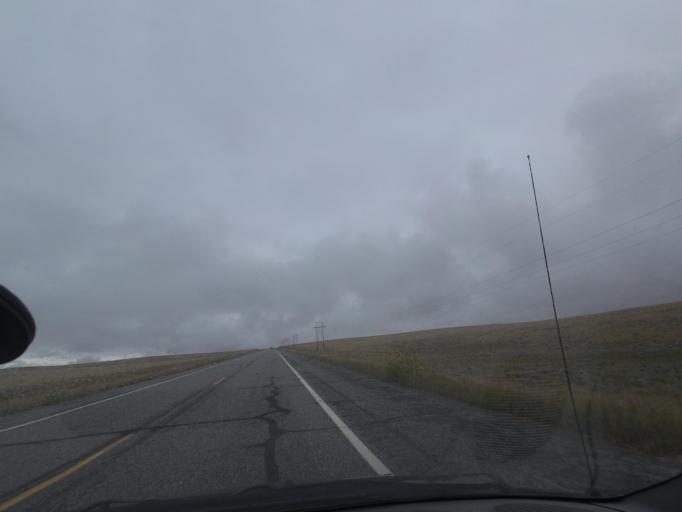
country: US
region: Colorado
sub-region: Lincoln County
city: Limon
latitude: 39.7399
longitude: -103.5431
